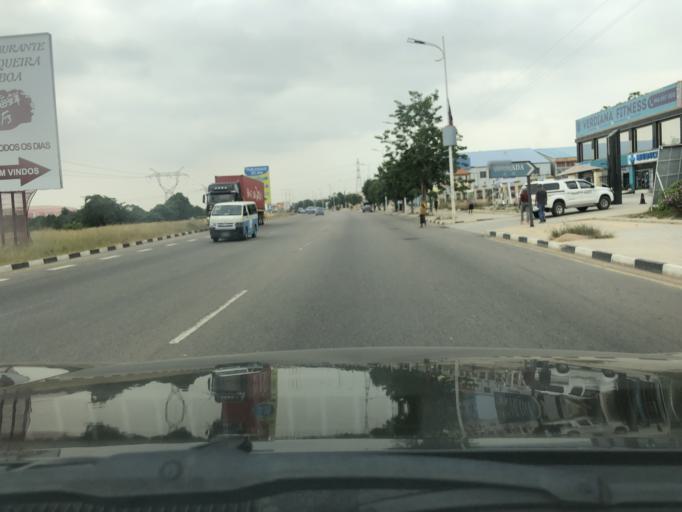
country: AO
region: Luanda
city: Luanda
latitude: -8.9789
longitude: 13.2899
